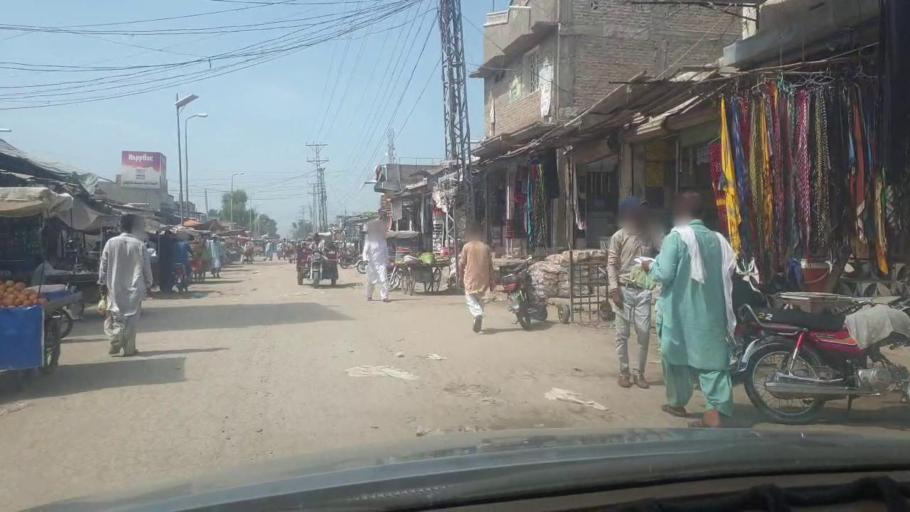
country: PK
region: Sindh
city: Gambat
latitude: 27.3021
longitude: 68.6121
